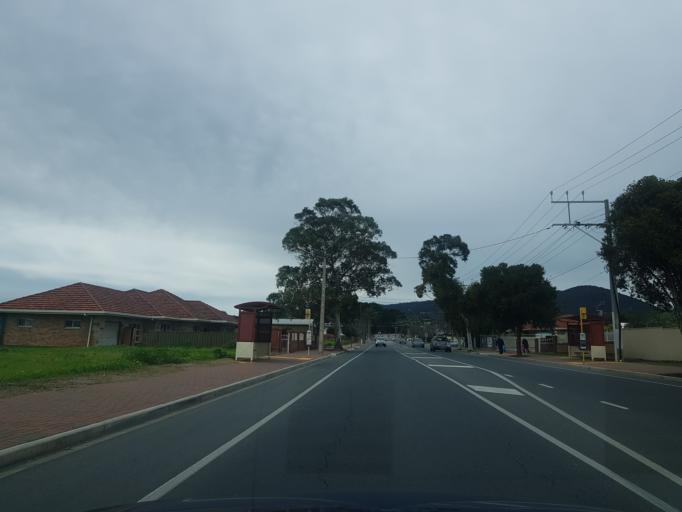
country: AU
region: South Australia
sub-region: Campbelltown
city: Paradise
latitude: -34.8760
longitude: 138.6803
